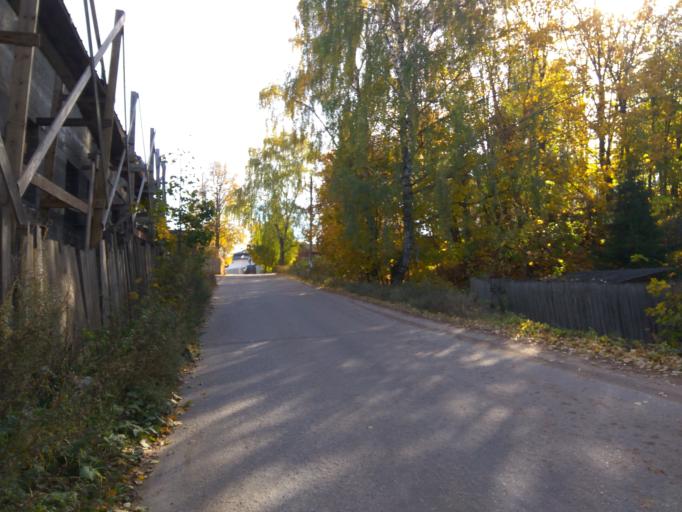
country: RU
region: Jaroslavl
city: Pereslavl'-Zalesskiy
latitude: 56.7209
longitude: 38.8342
